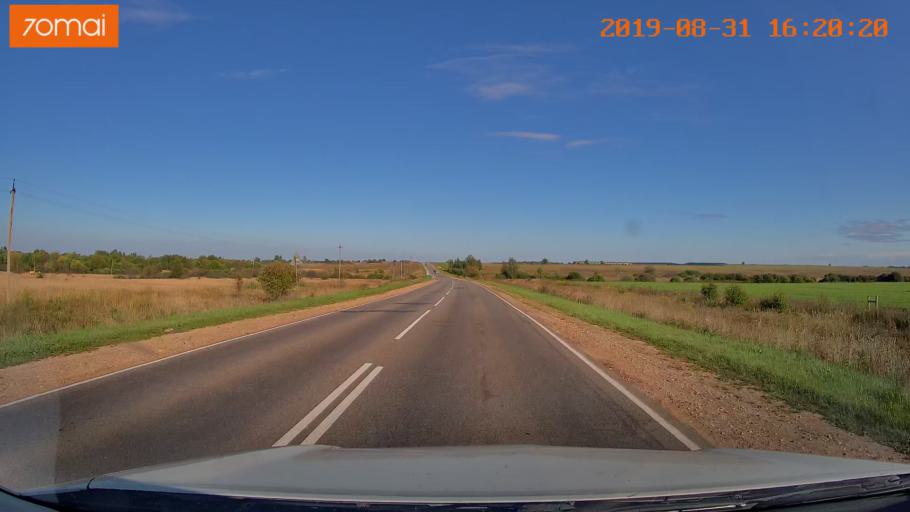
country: RU
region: Kaluga
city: Babynino
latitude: 54.5229
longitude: 35.6013
